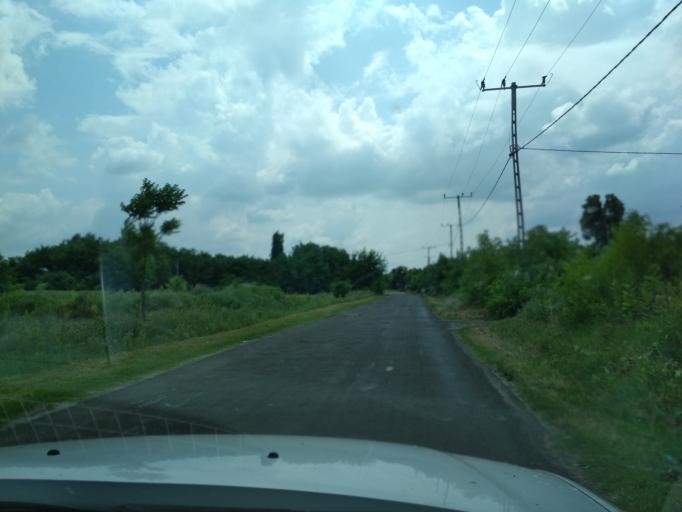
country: HU
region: Pest
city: Tapioszentmarton
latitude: 47.3765
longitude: 19.7566
